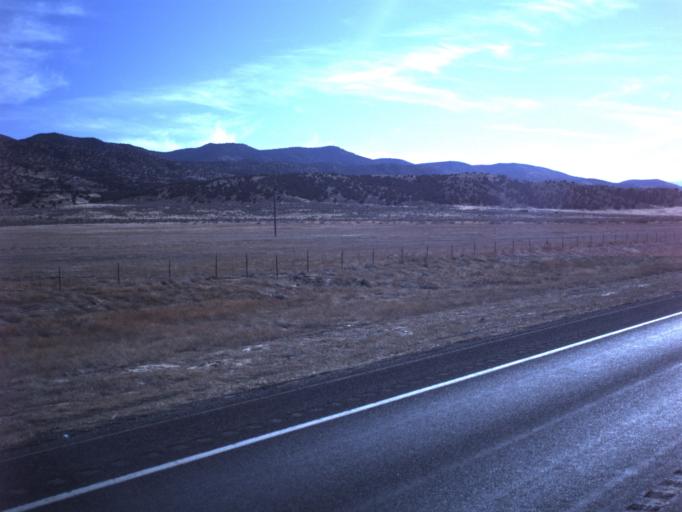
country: US
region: Utah
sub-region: Sanpete County
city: Gunnison
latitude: 39.3002
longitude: -111.8933
